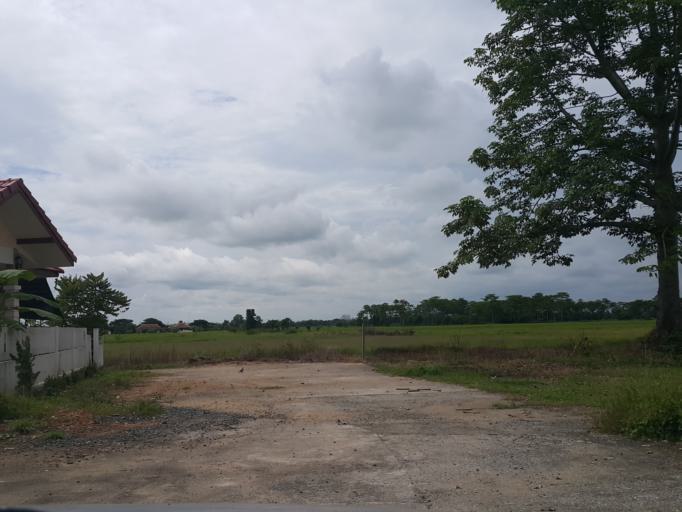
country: TH
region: Chiang Mai
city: San Kamphaeng
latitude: 18.8420
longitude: 99.1458
